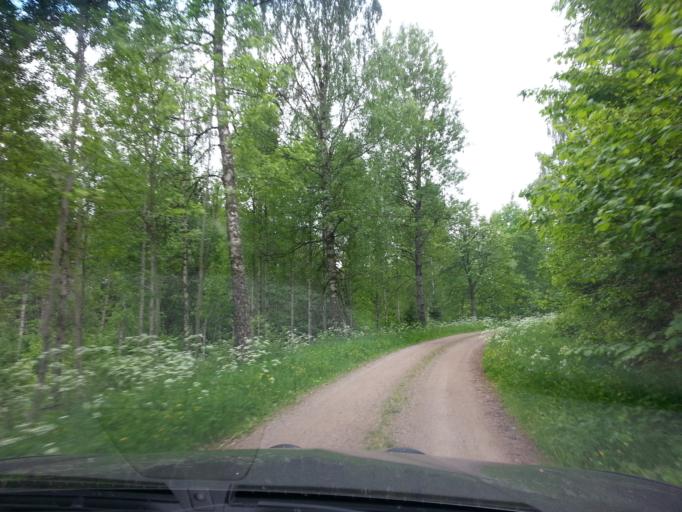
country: SE
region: Joenkoeping
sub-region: Vetlanda Kommun
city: Vetlanda
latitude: 57.2815
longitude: 15.1282
